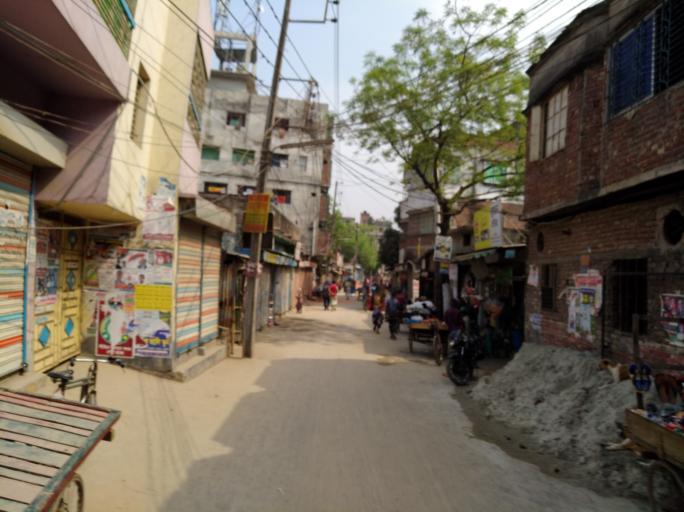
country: BD
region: Dhaka
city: Azimpur
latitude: 23.7155
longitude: 90.3765
